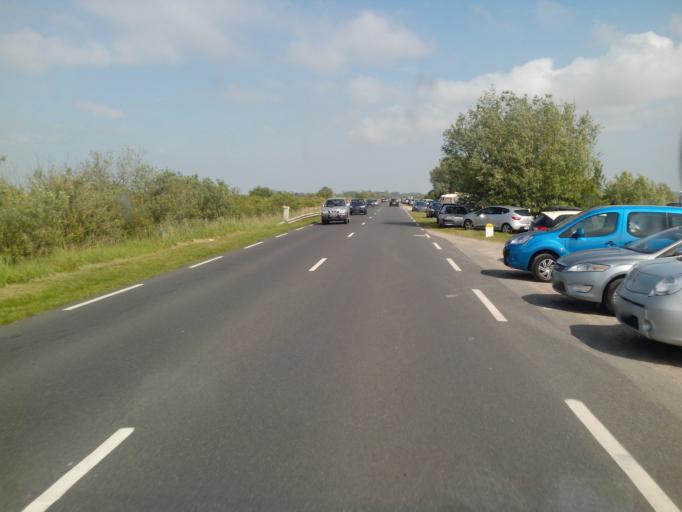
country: FR
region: Picardie
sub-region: Departement de la Somme
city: Le Crotoy
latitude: 50.2167
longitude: 1.6536
